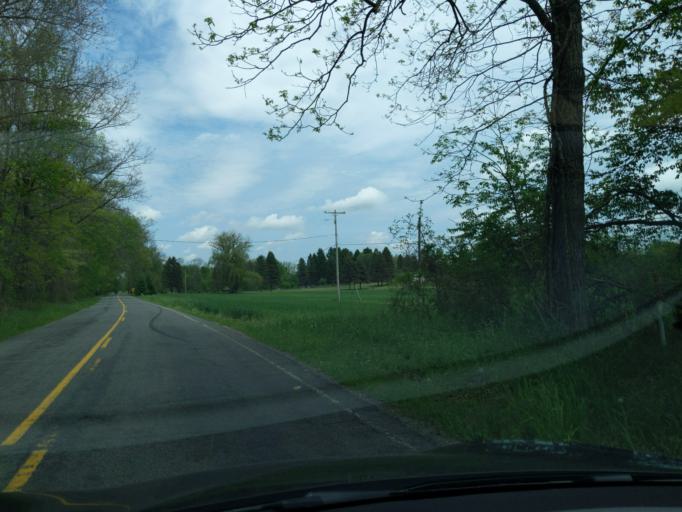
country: US
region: Michigan
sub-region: Ingham County
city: Stockbridge
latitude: 42.4648
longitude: -84.1769
